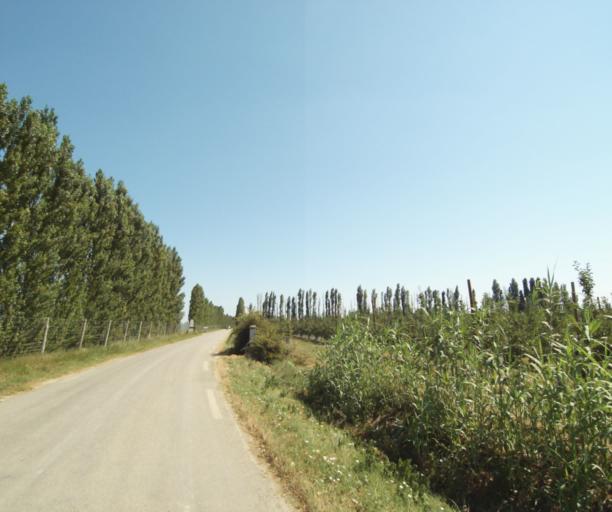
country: FR
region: Languedoc-Roussillon
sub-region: Departement de l'Herault
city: Marsillargues
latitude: 43.6457
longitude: 4.1693
